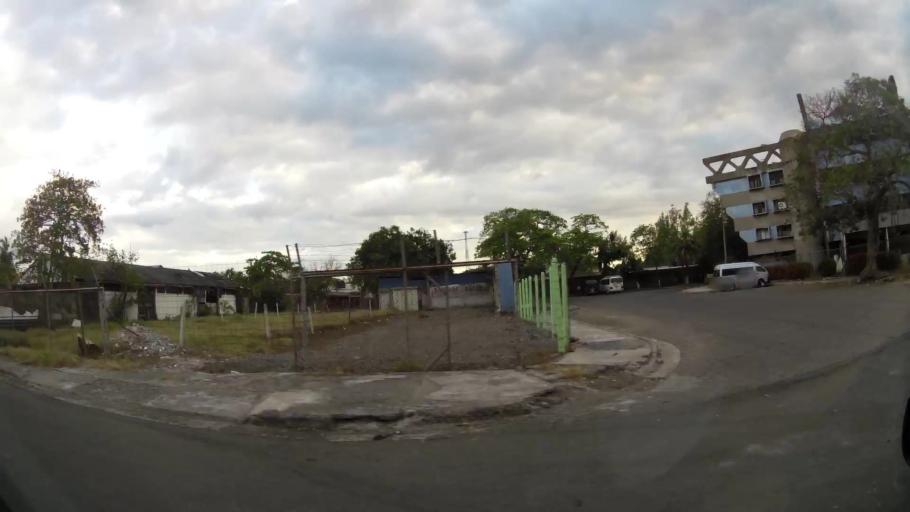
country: CR
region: Puntarenas
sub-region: Canton Central de Puntarenas
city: Puntarenas
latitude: 9.9796
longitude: -84.8359
